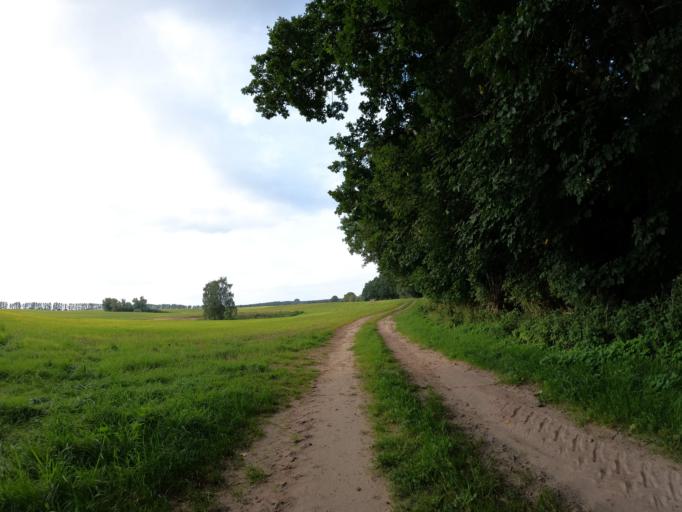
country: DE
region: Mecklenburg-Vorpommern
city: Klink
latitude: 53.4442
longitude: 12.5251
